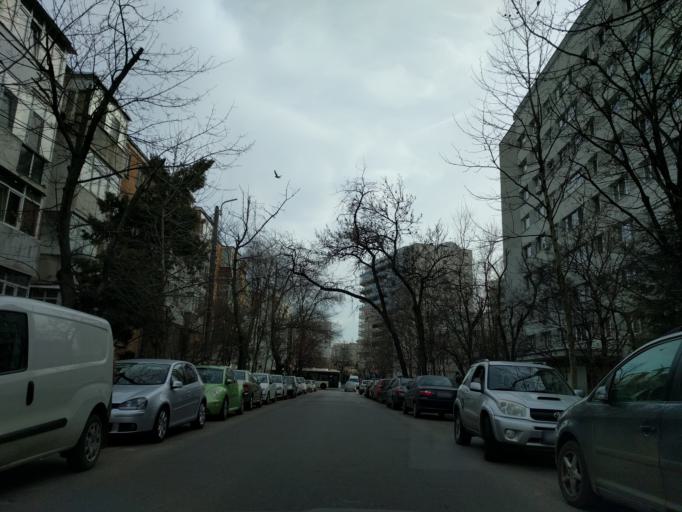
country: RO
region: Bucuresti
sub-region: Municipiul Bucuresti
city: Bucharest
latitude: 44.4257
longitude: 26.1415
